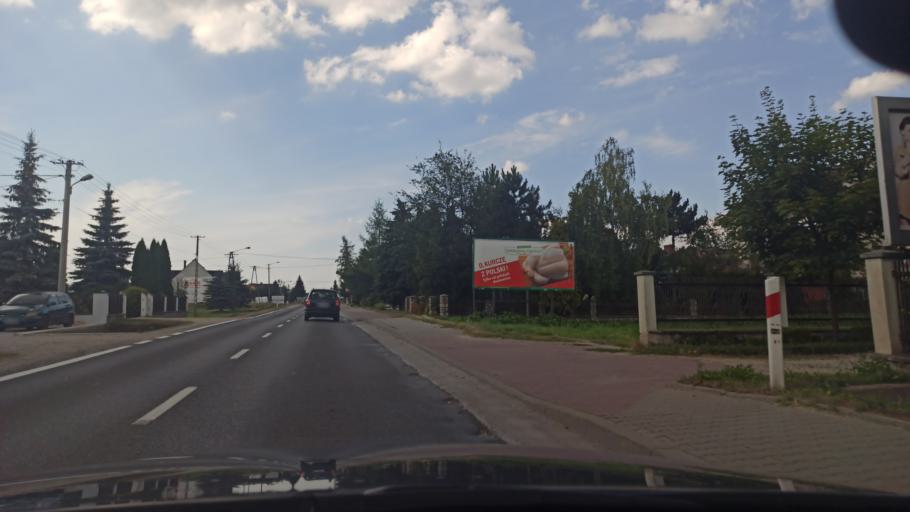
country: PL
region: Lesser Poland Voivodeship
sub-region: Powiat nowotarski
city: Ostrowsko
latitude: 49.4771
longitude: 20.0938
